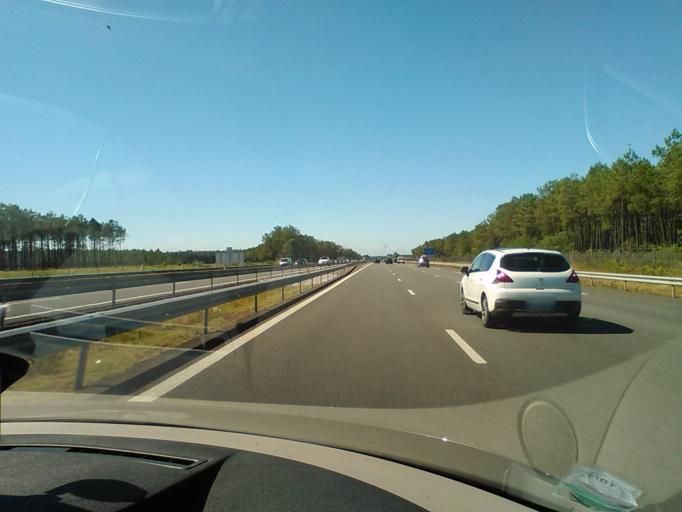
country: FR
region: Aquitaine
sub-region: Departement des Landes
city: Magescq
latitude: 43.8132
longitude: -1.1951
